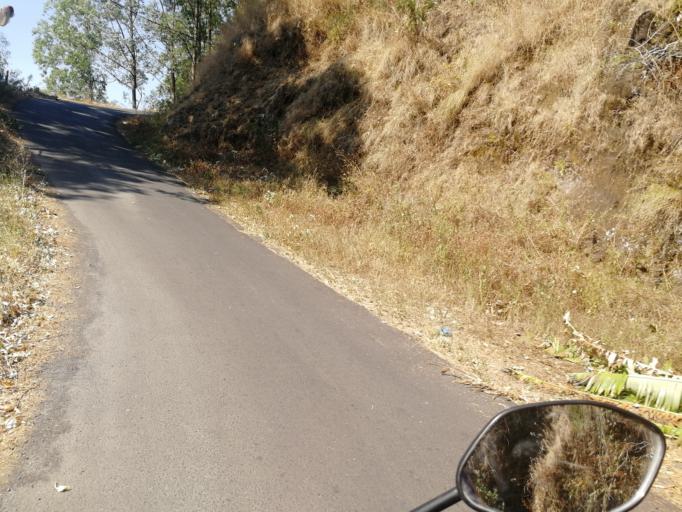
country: ID
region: Bali
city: Banjar Trunyan
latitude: -8.2565
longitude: 115.4241
